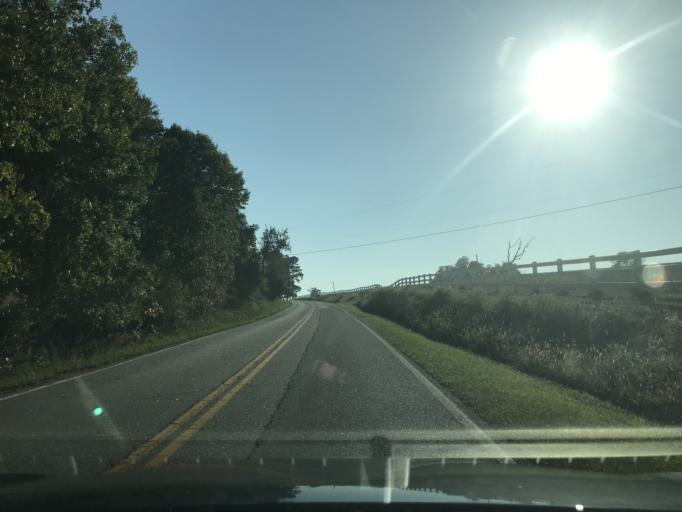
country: US
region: South Carolina
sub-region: Spartanburg County
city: Mayo
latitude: 35.1318
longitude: -81.7711
